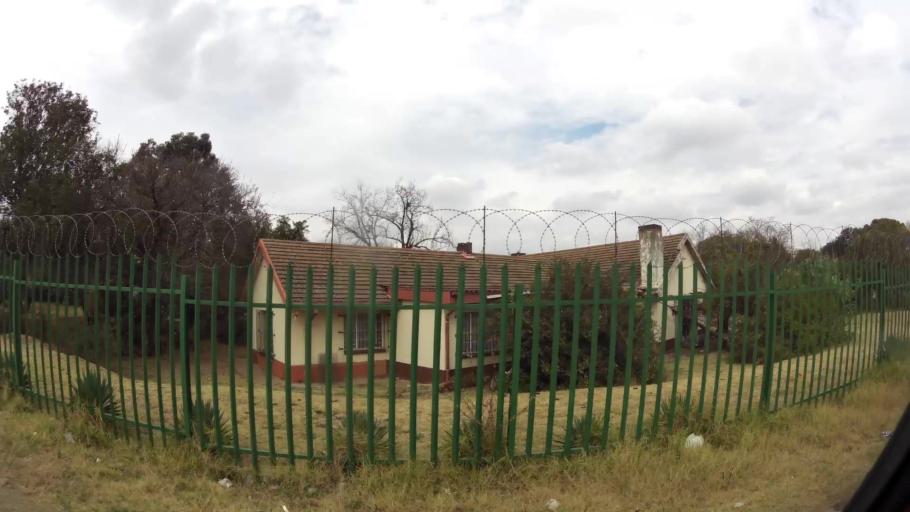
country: ZA
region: Gauteng
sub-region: West Rand District Municipality
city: Muldersdriseloop
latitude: -26.0739
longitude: 27.9139
